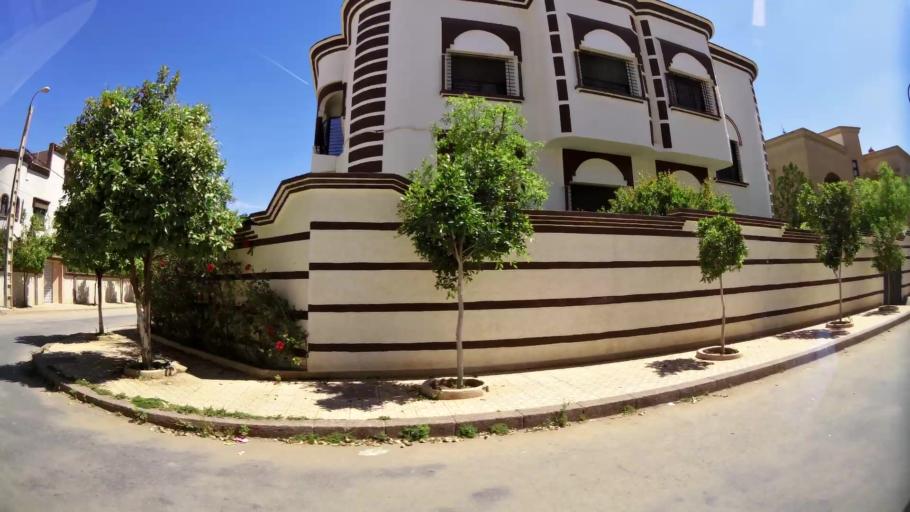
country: MA
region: Oriental
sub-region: Oujda-Angad
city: Oujda
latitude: 34.6636
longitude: -1.9313
